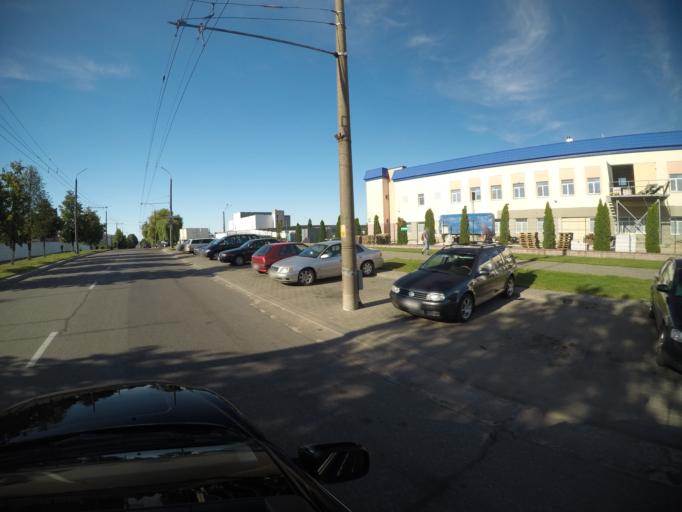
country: BY
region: Grodnenskaya
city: Hrodna
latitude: 53.7093
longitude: 23.8274
